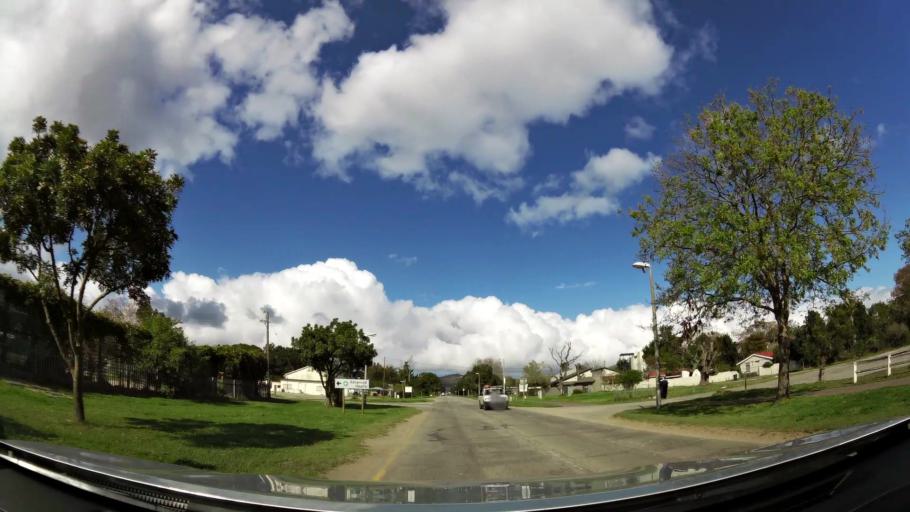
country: ZA
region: Western Cape
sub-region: Eden District Municipality
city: Knysna
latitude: -34.0487
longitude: 23.0700
